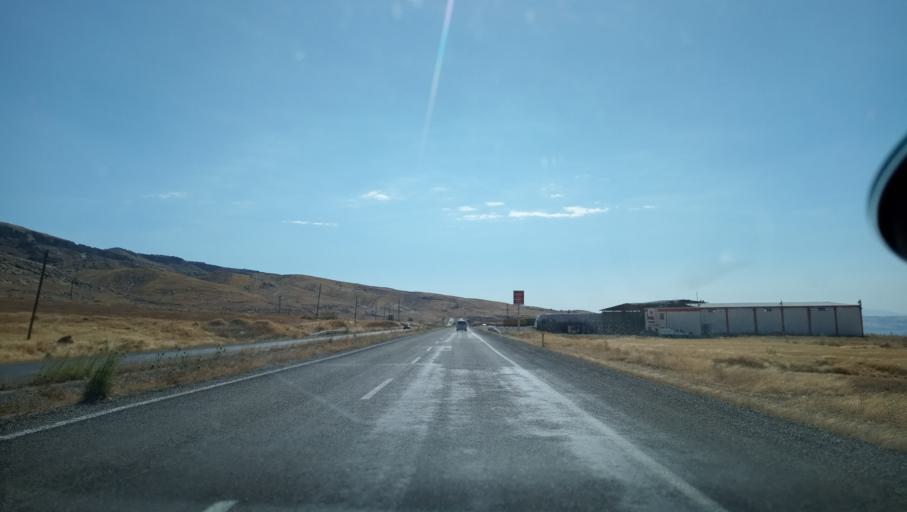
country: TR
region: Diyarbakir
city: Silvan
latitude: 38.1279
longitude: 41.0713
